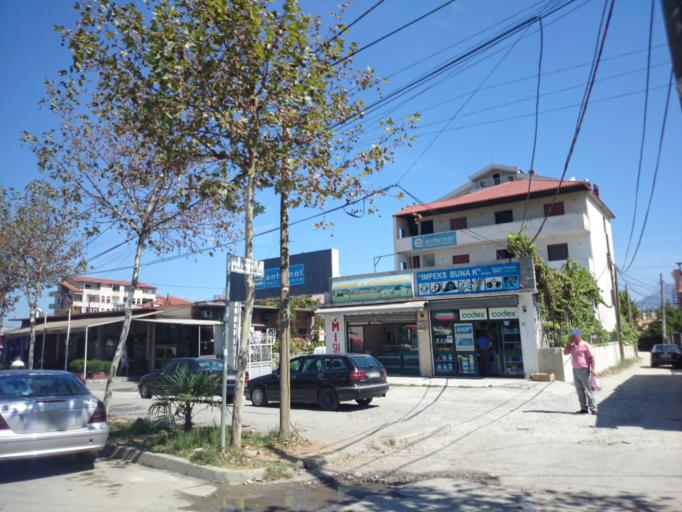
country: AL
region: Tirane
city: Tirana
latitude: 41.3230
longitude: 19.7889
